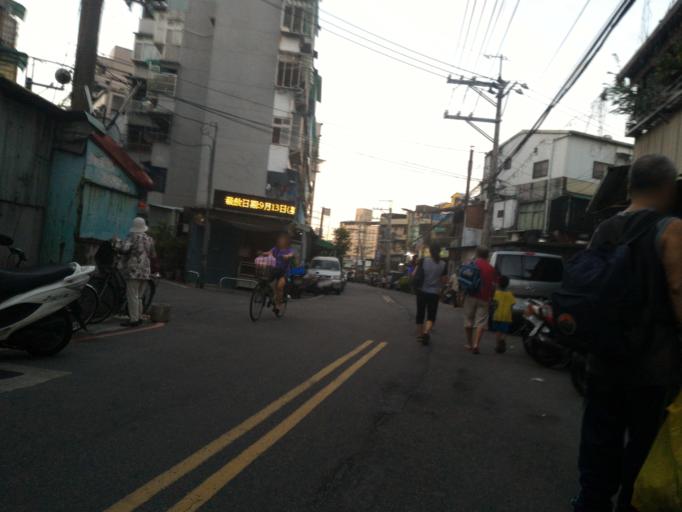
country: TW
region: Taipei
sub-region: Taipei
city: Banqiao
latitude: 24.9769
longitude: 121.4185
